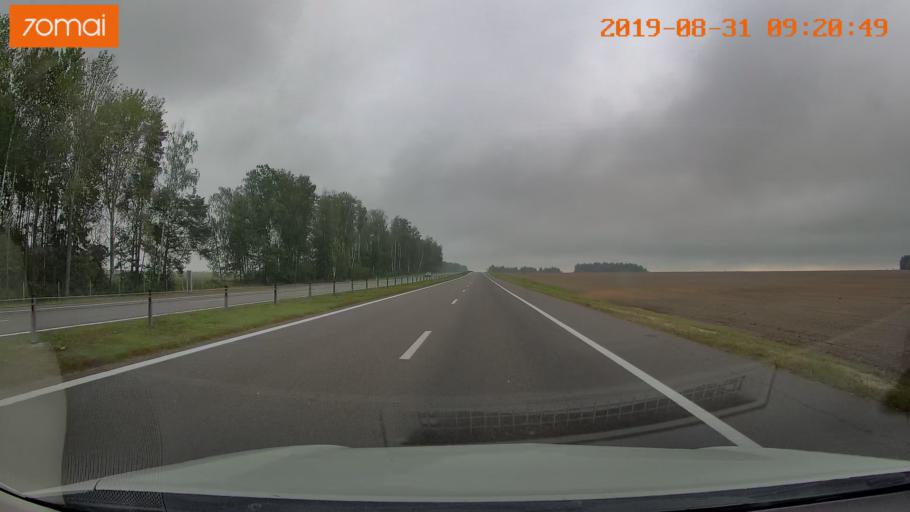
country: BY
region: Minsk
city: Byerazino
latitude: 53.7973
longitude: 28.8408
